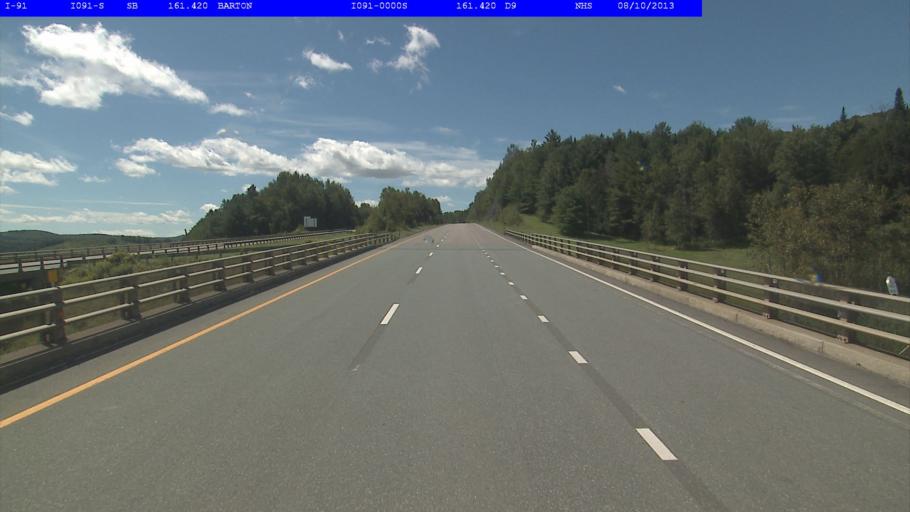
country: US
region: Vermont
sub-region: Orleans County
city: Newport
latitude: 44.8067
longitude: -72.2125
